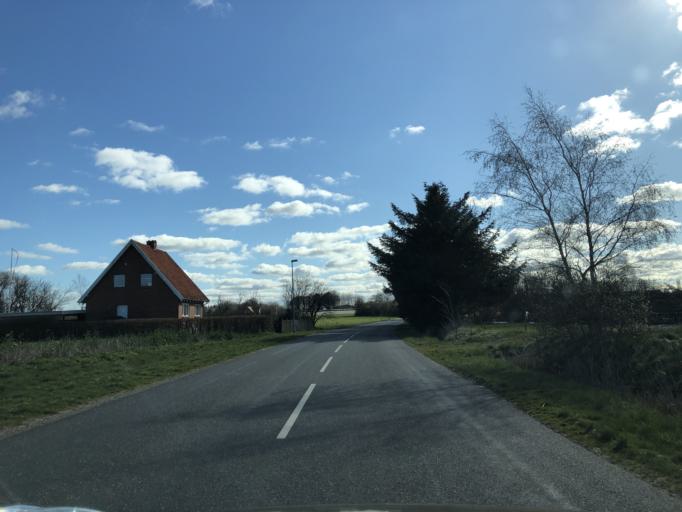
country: DK
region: North Denmark
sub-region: Vesthimmerland Kommune
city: Alestrup
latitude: 56.6071
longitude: 9.5491
